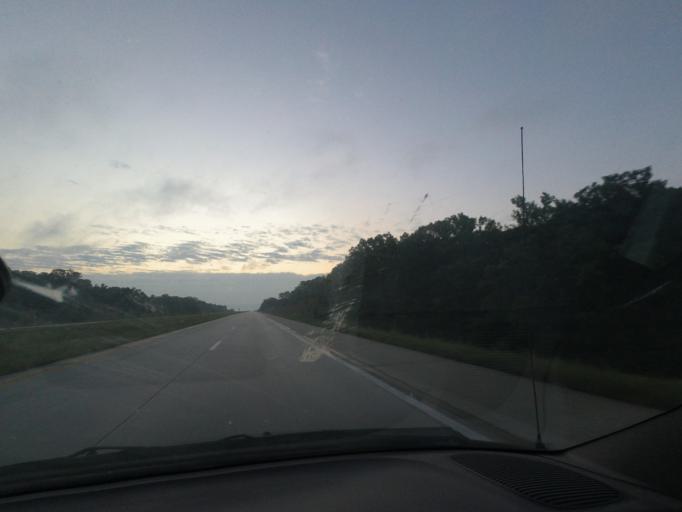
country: US
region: Missouri
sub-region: Linn County
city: Marceline
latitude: 39.7590
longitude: -92.8398
